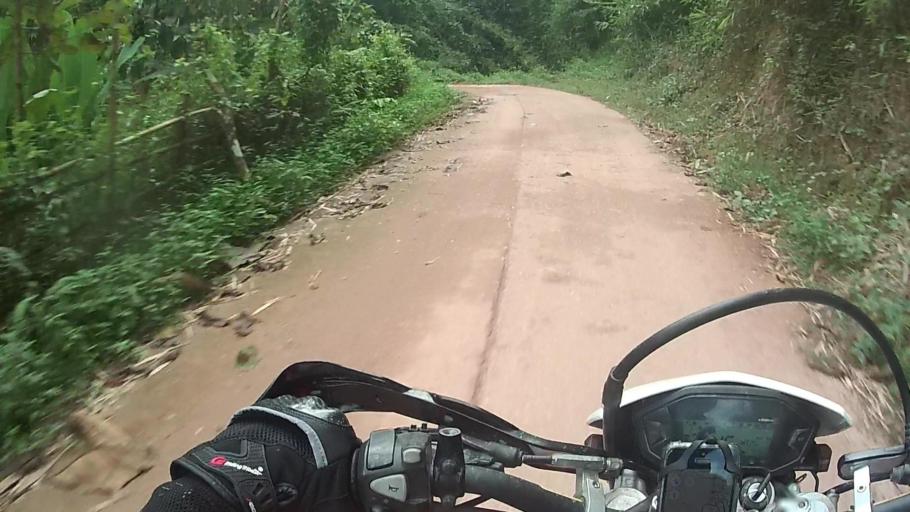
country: TH
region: Lampang
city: Mueang Pan
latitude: 18.9728
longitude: 99.5048
